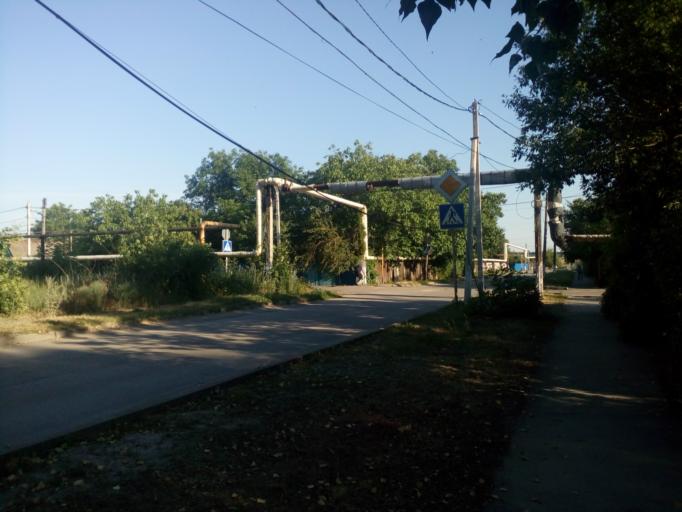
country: RU
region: Rostov
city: Sholokhovskiy
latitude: 48.2787
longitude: 41.0420
